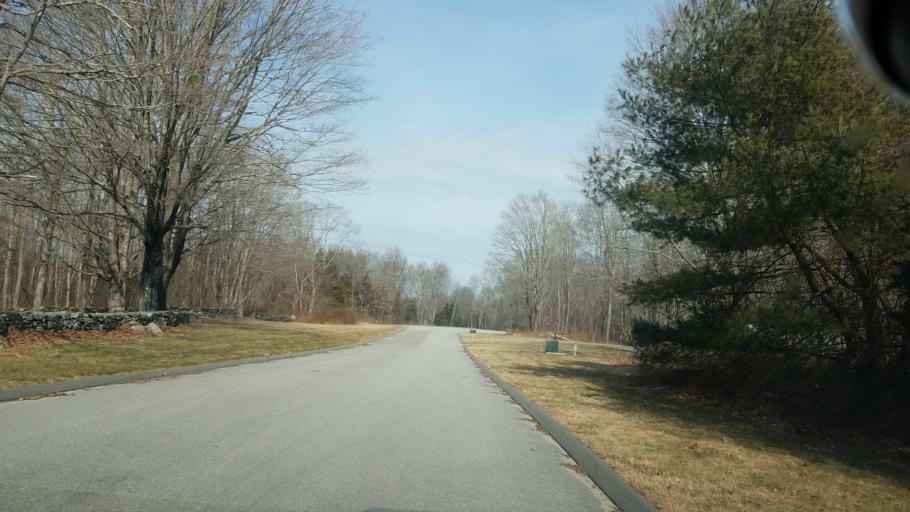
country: US
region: Connecticut
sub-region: New London County
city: Preston City
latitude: 41.5023
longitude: -72.0057
